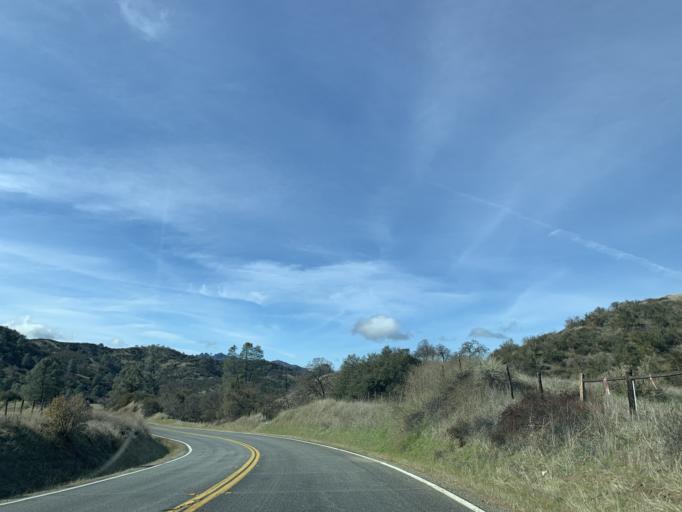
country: US
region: California
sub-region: Monterey County
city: Greenfield
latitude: 36.5072
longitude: -121.1052
